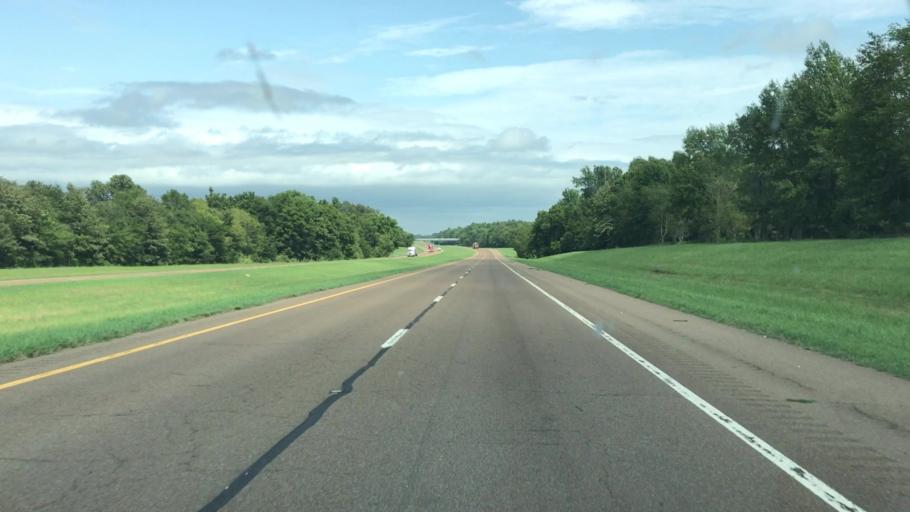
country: US
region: Tennessee
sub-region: Obion County
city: South Fulton
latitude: 36.4783
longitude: -88.9507
